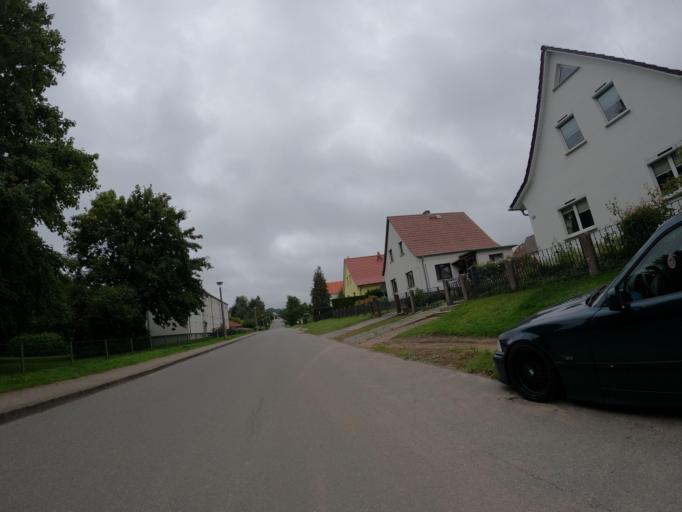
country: DE
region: Mecklenburg-Vorpommern
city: Putbus
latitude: 54.3497
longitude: 13.4830
